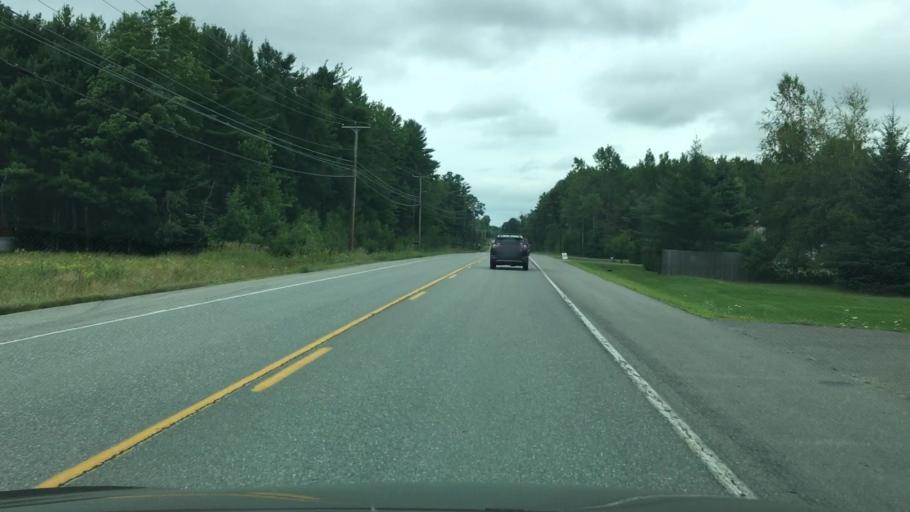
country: US
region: Maine
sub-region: Penobscot County
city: Orrington
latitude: 44.7048
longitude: -68.8230
